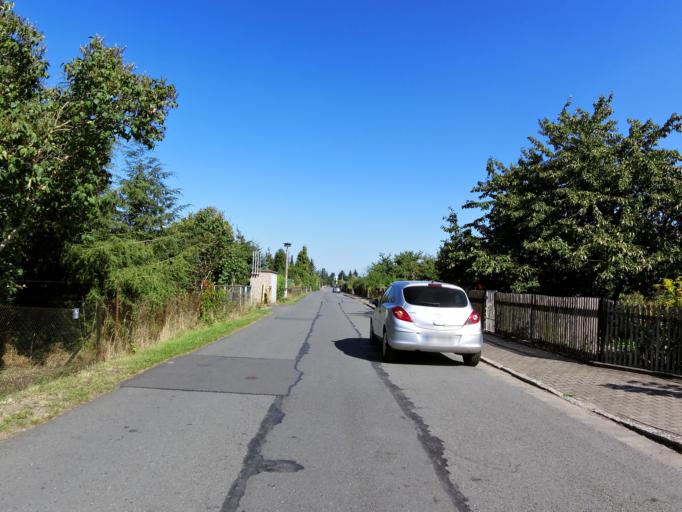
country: DE
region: Saxony
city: Riesa
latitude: 51.3281
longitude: 13.2968
